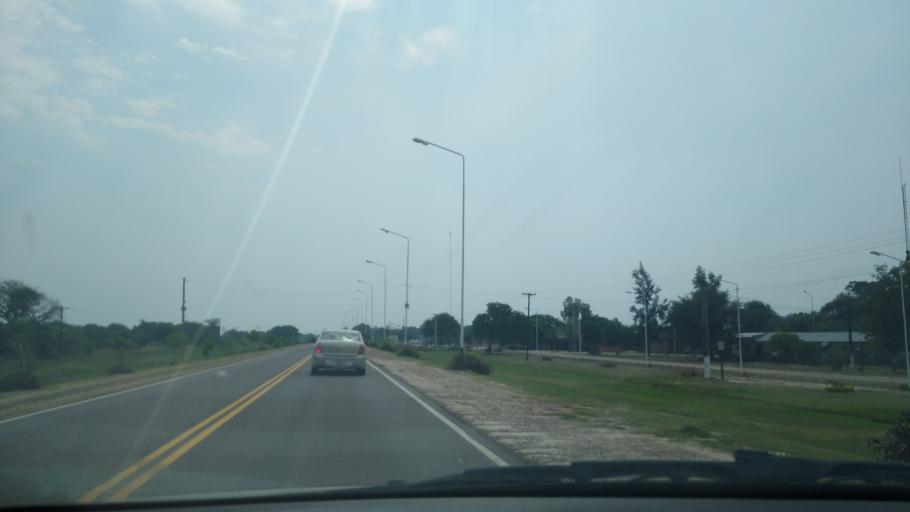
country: AR
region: Chaco
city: La Eduvigis
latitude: -26.8369
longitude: -59.0640
